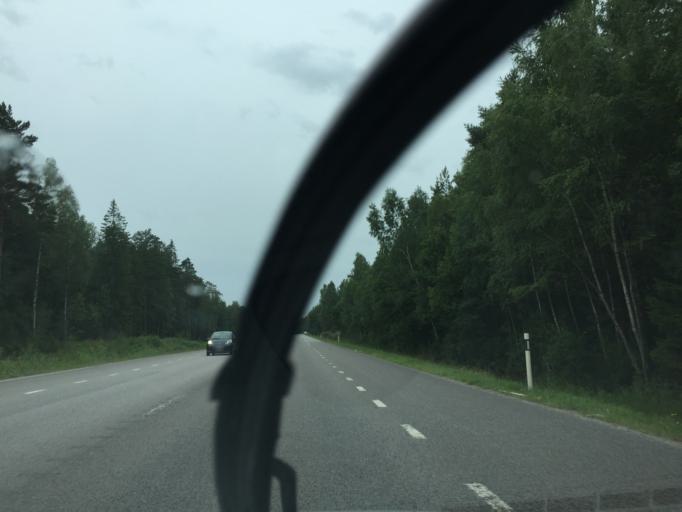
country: SE
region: OErebro
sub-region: Orebro Kommun
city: Orebro
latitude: 59.2366
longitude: 15.2312
